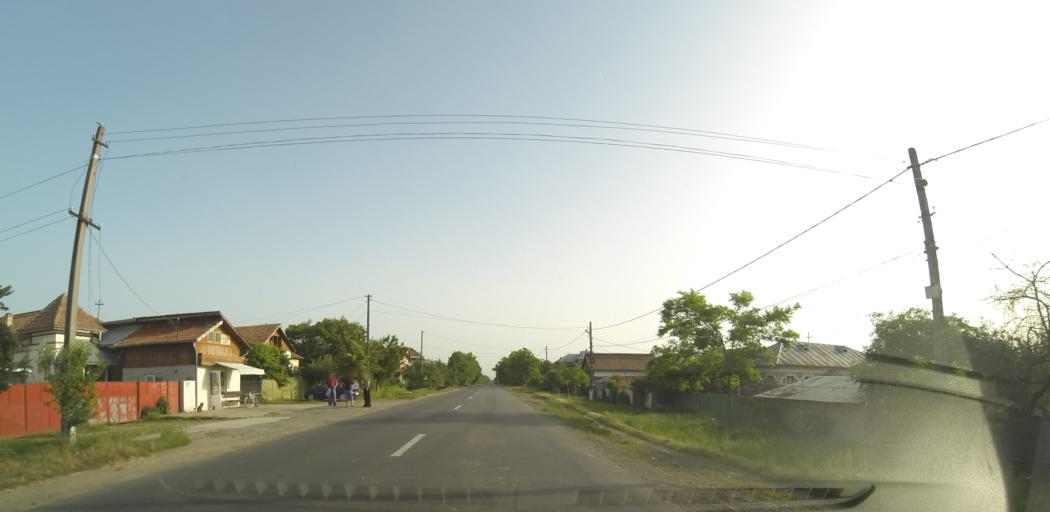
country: RO
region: Valcea
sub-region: Comuna Orlesti
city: Orlesti
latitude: 44.8085
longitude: 24.2458
